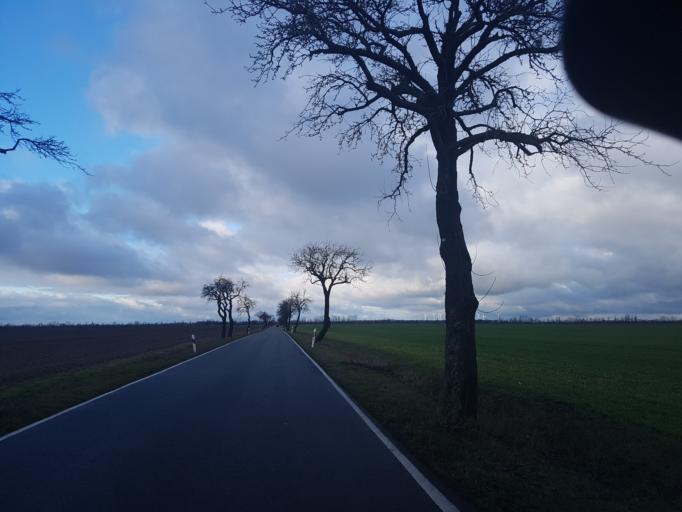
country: DE
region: Brandenburg
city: Muhlberg
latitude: 51.4055
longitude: 13.2415
